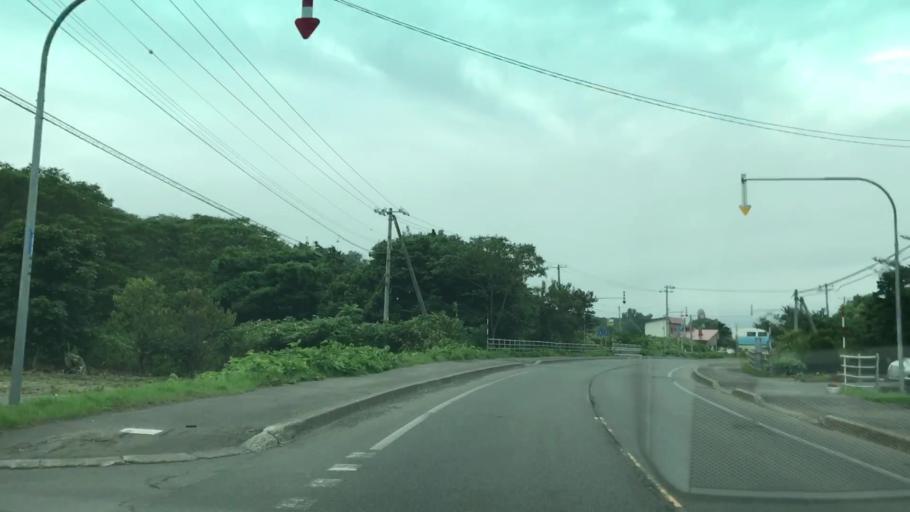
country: JP
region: Hokkaido
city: Iwanai
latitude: 42.7730
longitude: 140.3047
